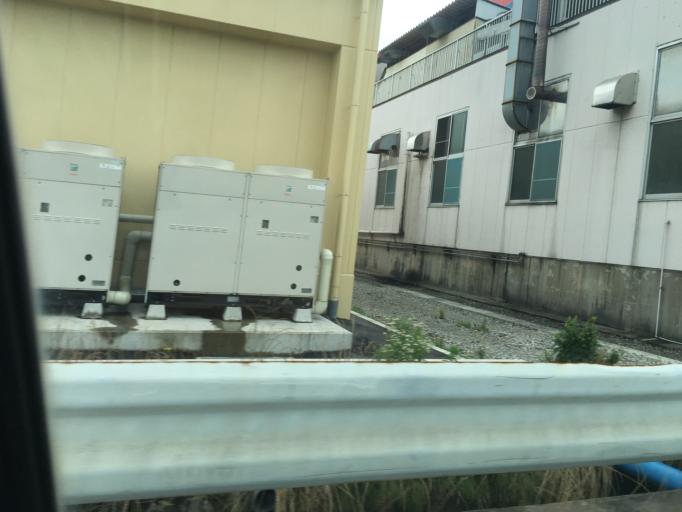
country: JP
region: Aichi
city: Ishiki
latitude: 34.8080
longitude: 137.0197
